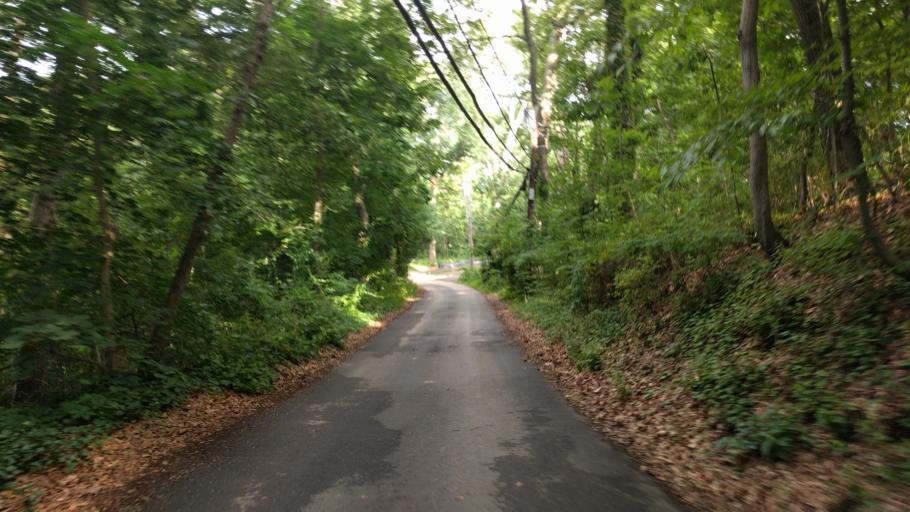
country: US
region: New York
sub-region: Nassau County
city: Oyster Bay Cove
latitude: 40.8707
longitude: -73.4925
